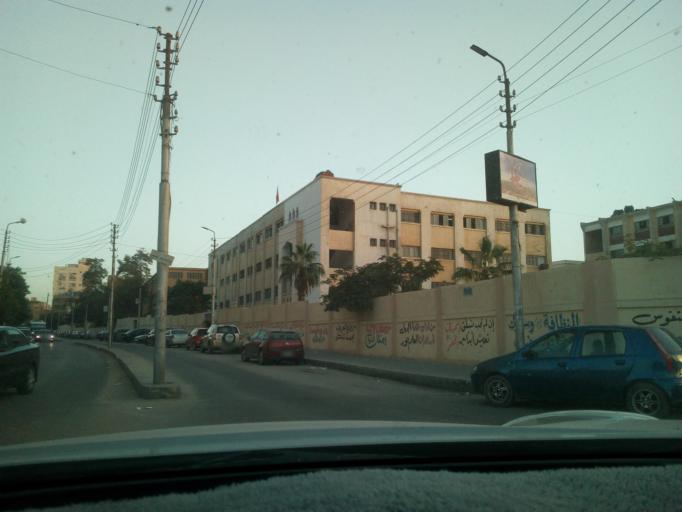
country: EG
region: Muhafazat al Qahirah
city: Cairo
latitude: 30.0914
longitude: 31.3433
